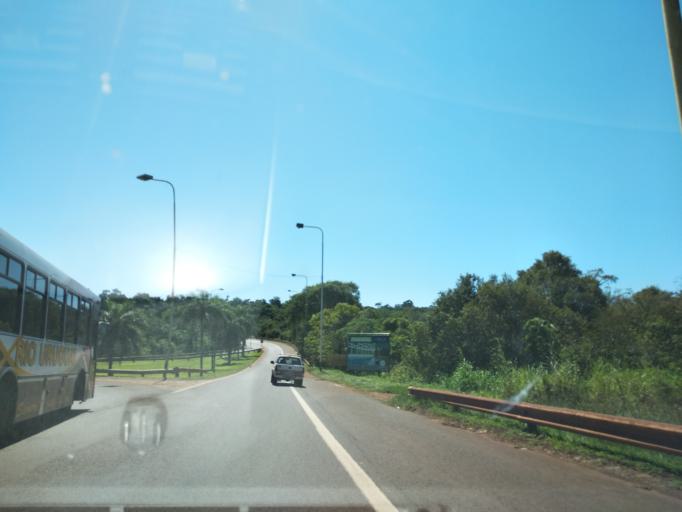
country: AR
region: Misiones
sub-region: Departamento de Iguazu
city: Puerto Iguazu
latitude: -25.6116
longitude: -54.5609
